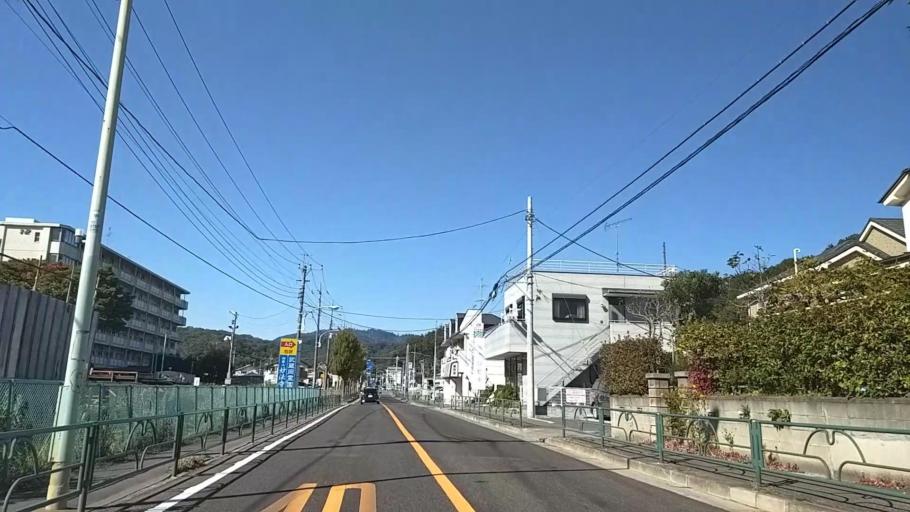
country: JP
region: Tokyo
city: Hachioji
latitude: 35.6099
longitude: 139.2982
